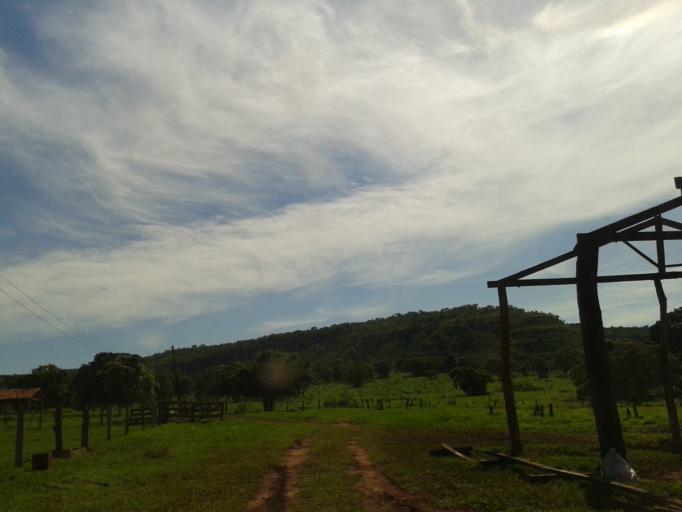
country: BR
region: Minas Gerais
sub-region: Santa Vitoria
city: Santa Vitoria
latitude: -19.0837
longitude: -50.0148
